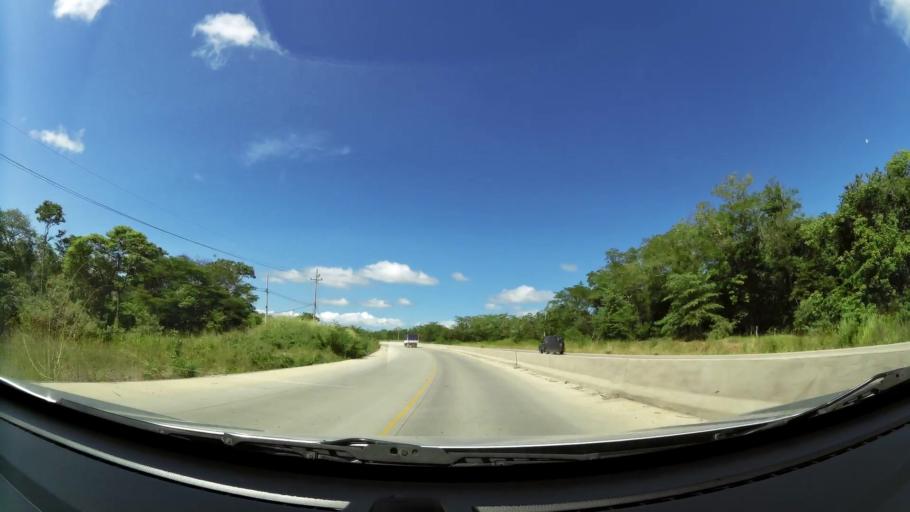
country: CR
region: Guanacaste
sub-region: Canton de Canas
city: Canas
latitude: 10.4451
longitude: -85.1136
